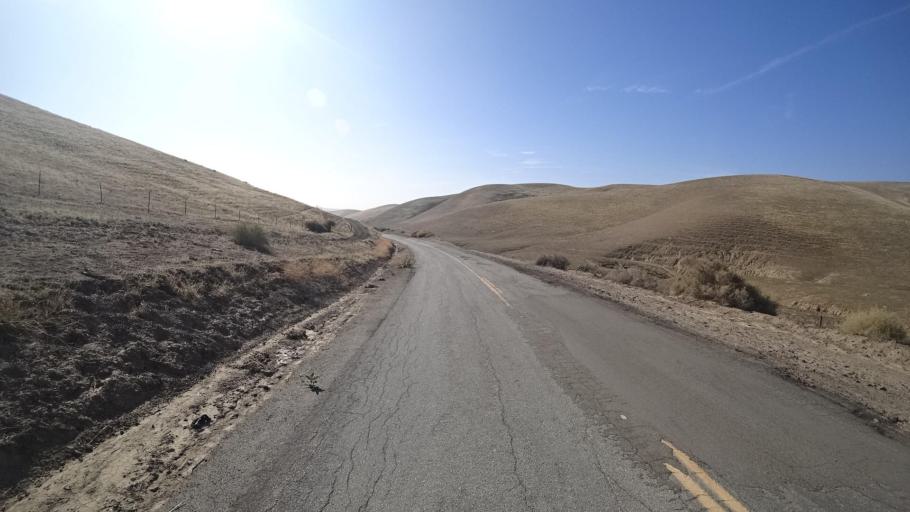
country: US
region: California
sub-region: Kern County
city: Oildale
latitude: 35.4597
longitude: -118.8272
